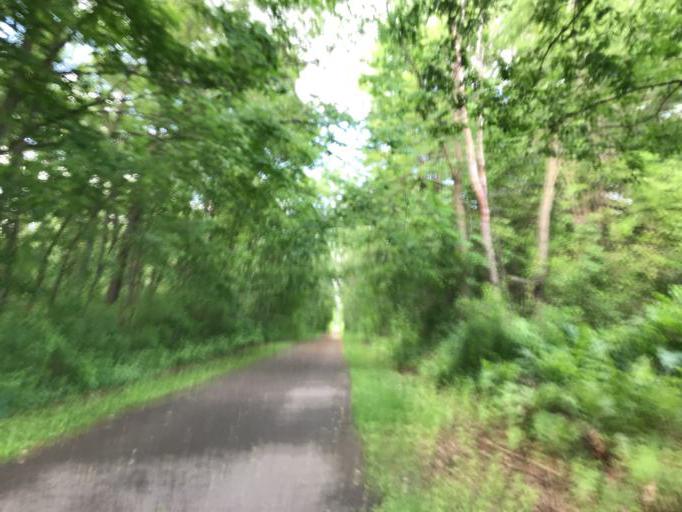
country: US
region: Michigan
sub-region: Oakland County
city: South Lyon
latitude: 42.4791
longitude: -83.6408
